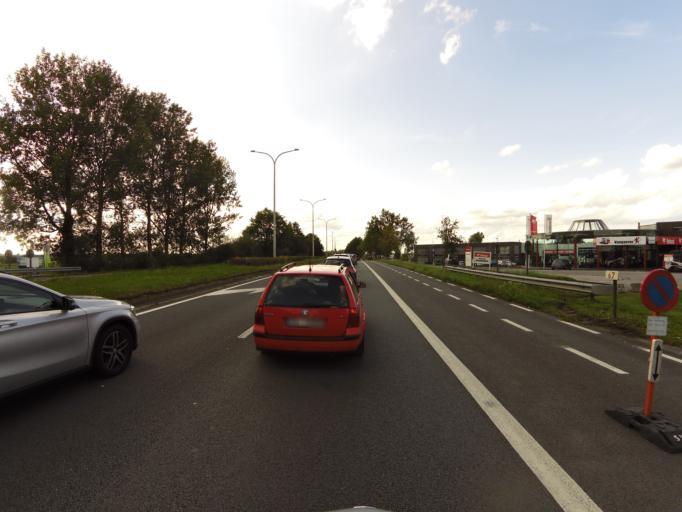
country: BE
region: Flanders
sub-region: Provincie West-Vlaanderen
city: Waregem
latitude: 50.8741
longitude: 3.4380
